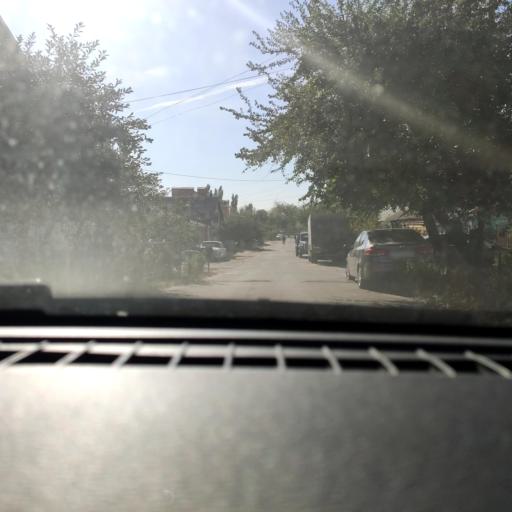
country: RU
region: Voronezj
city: Voronezh
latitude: 51.6691
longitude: 39.2654
